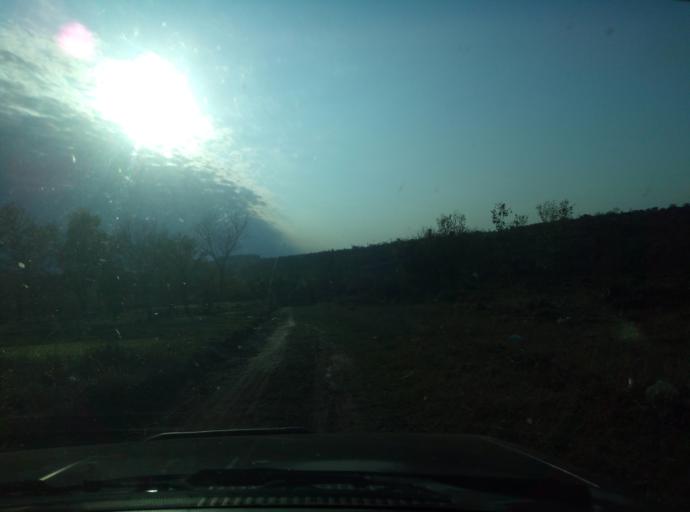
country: PY
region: Caaguazu
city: Yhu
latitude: -25.1990
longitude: -56.1158
